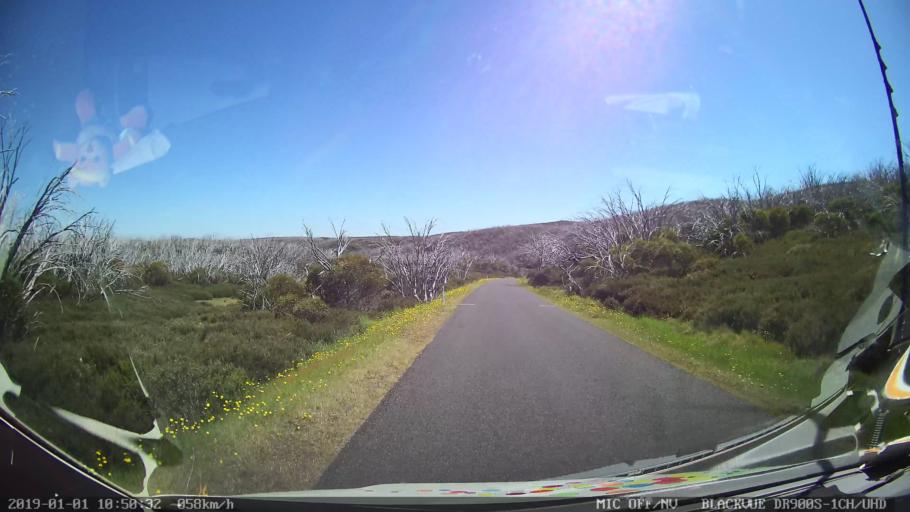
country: AU
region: New South Wales
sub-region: Snowy River
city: Jindabyne
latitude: -36.0275
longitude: 148.3711
